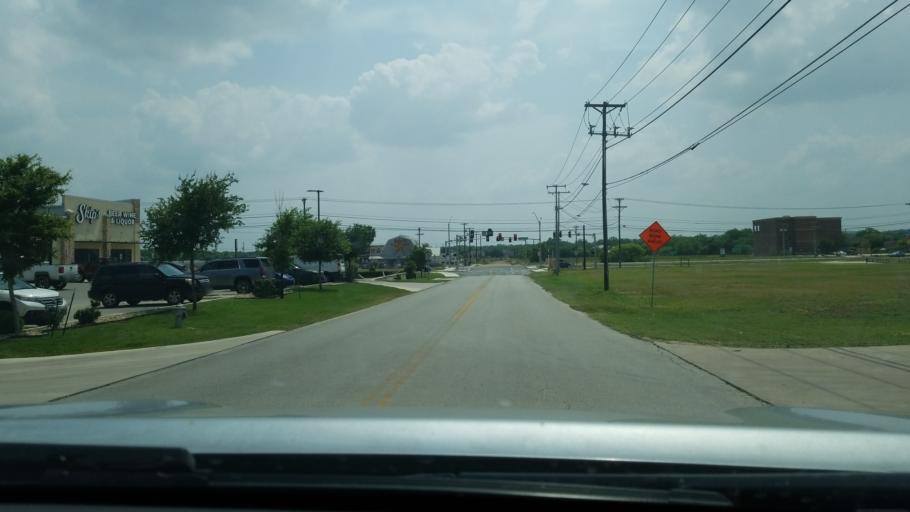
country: US
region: Texas
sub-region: Comal County
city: New Braunfels
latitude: 29.7255
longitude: -98.1070
